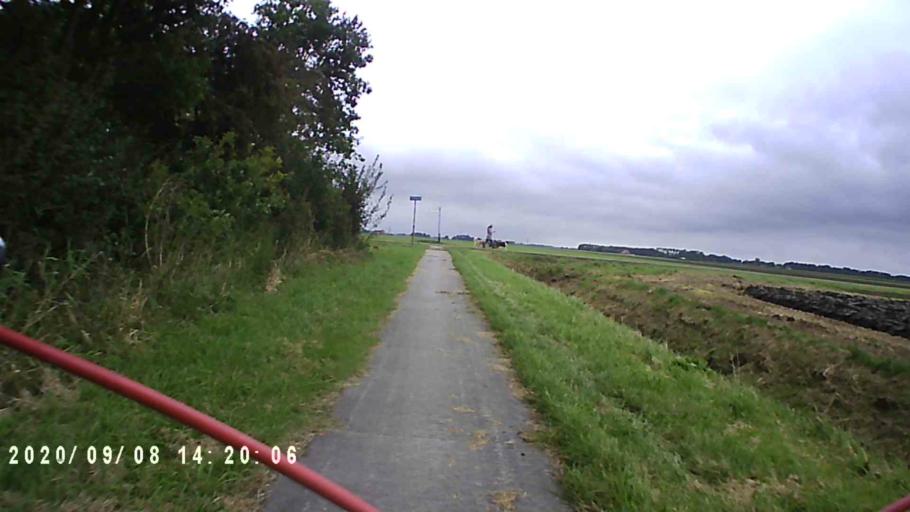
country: NL
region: Groningen
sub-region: Gemeente Slochteren
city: Slochteren
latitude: 53.2094
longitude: 6.8474
